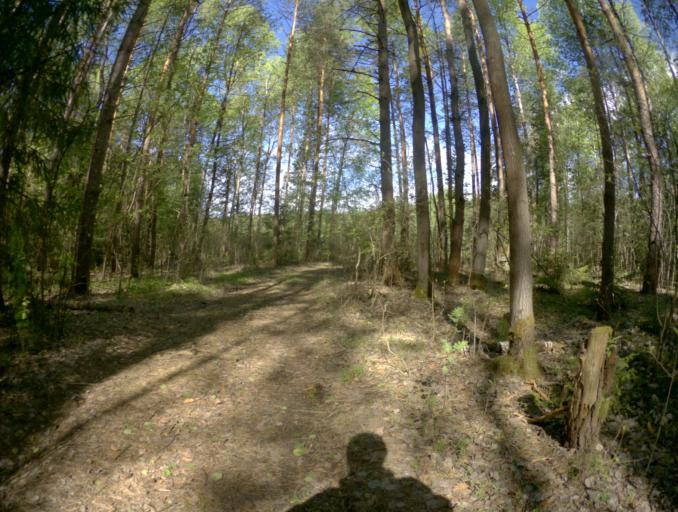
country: RU
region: Rjazan
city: Spas-Klepiki
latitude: 55.2484
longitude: 40.0948
